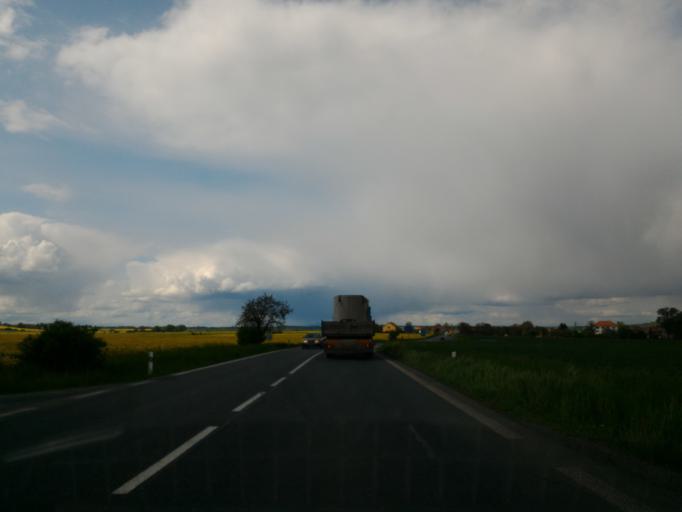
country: CZ
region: Central Bohemia
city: Lustenice
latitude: 50.3460
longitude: 14.9168
